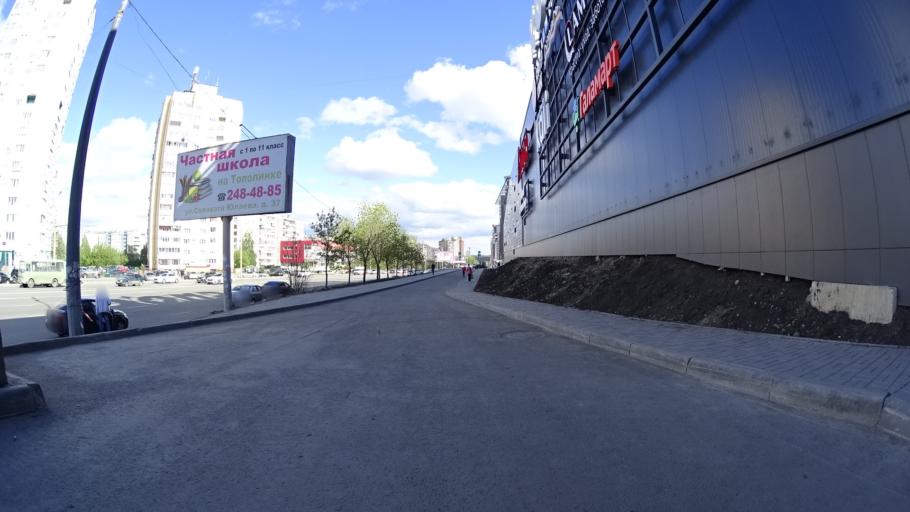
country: RU
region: Chelyabinsk
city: Roshchino
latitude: 55.1815
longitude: 61.2932
